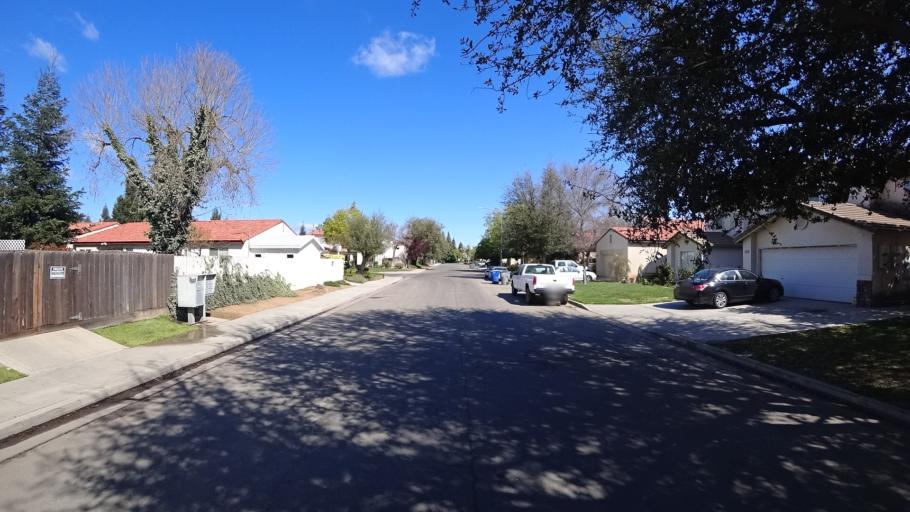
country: US
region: California
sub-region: Fresno County
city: West Park
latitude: 36.7878
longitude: -119.8866
